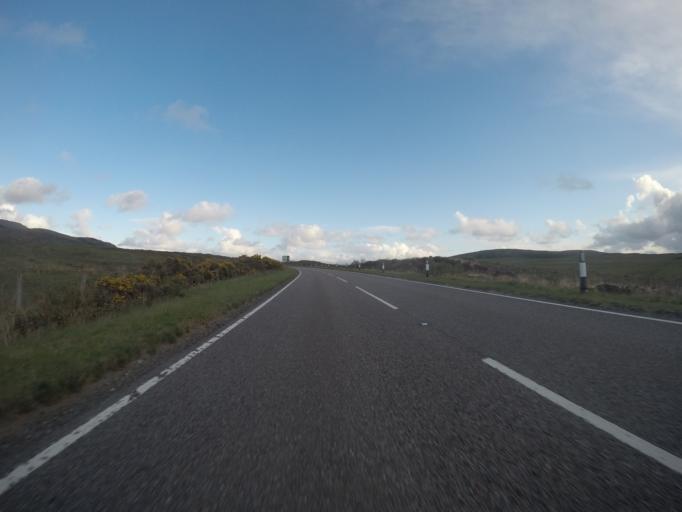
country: GB
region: Scotland
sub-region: Highland
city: Portree
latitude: 57.4759
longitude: -6.2997
